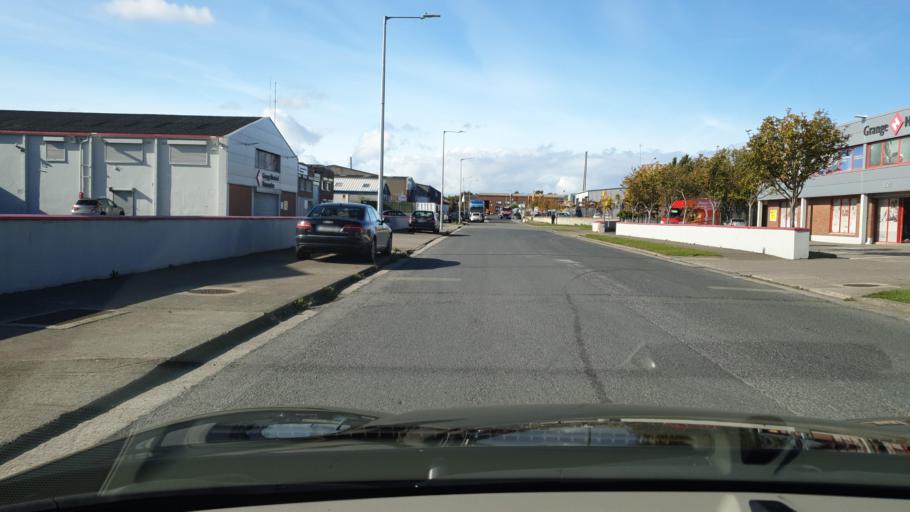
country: IE
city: Bayside
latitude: 53.3963
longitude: -6.1463
